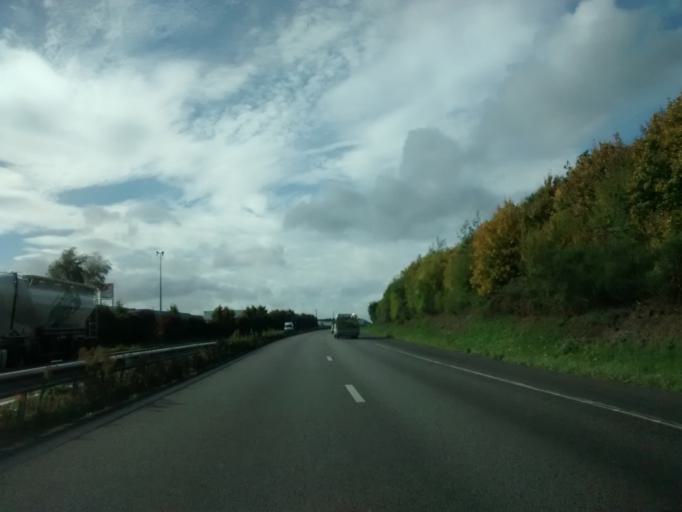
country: FR
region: Brittany
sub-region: Departement d'Ille-et-Vilaine
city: Noyal-sur-Vilaine
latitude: 48.1082
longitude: -1.5243
